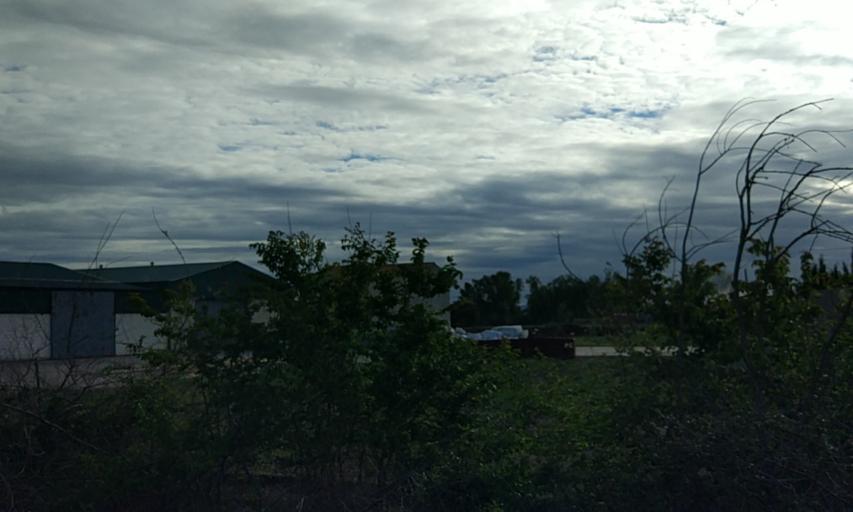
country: ES
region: Extremadura
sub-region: Provincia de Caceres
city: Moraleja
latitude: 40.0818
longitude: -6.6700
